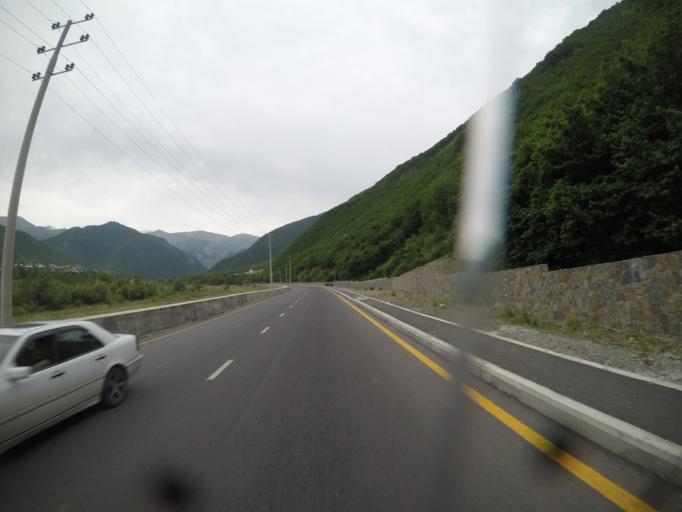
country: AZ
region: Shaki City
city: Sheki
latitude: 41.2419
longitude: 47.1927
